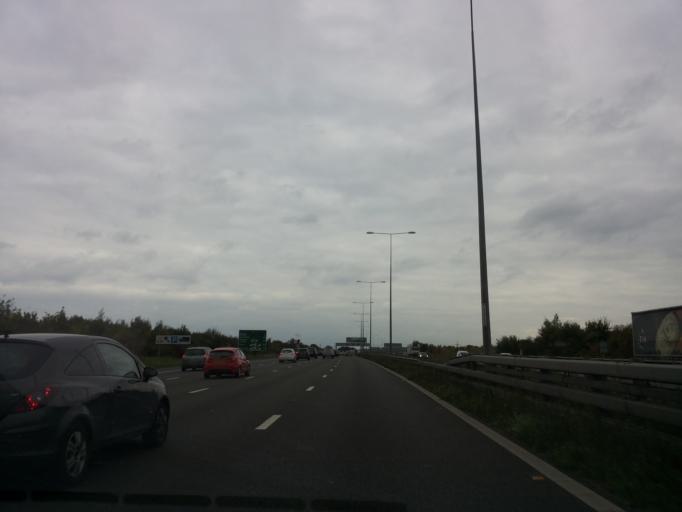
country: GB
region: England
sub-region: Kent
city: Gravesend
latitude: 51.4134
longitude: 0.3666
